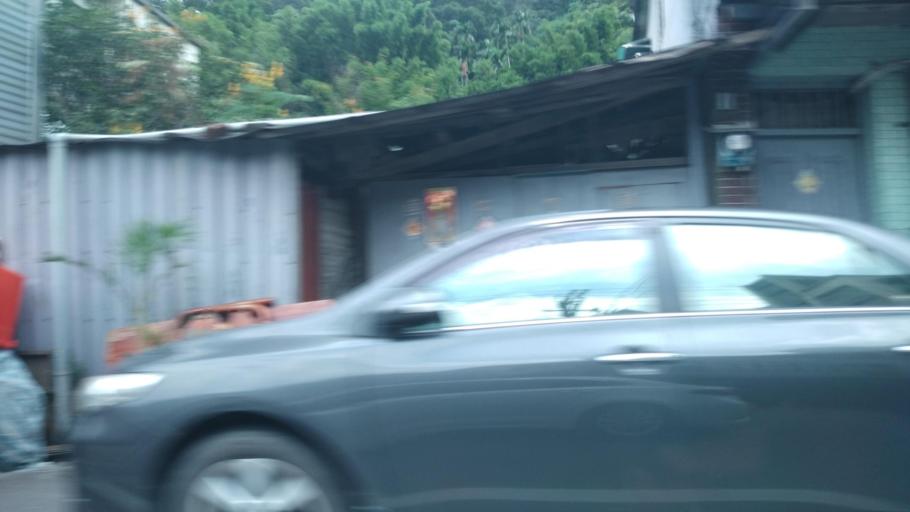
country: TW
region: Taipei
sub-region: Taipei
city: Banqiao
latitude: 24.9498
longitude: 121.4831
